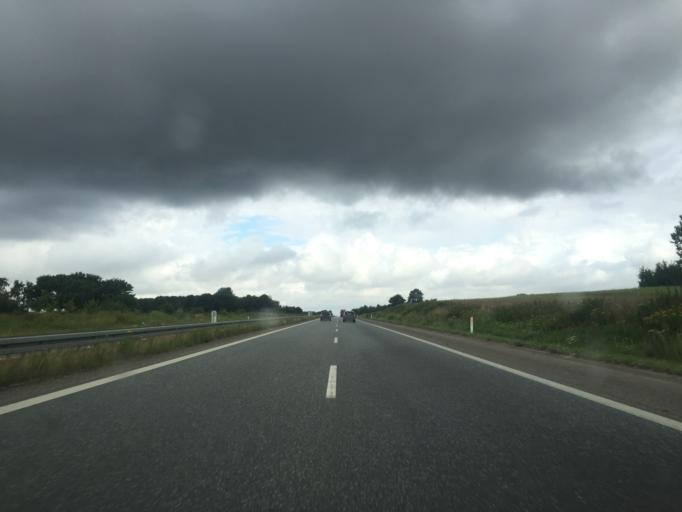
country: DK
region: South Denmark
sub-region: Faaborg-Midtfyn Kommune
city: Ringe
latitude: 55.2057
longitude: 10.5114
